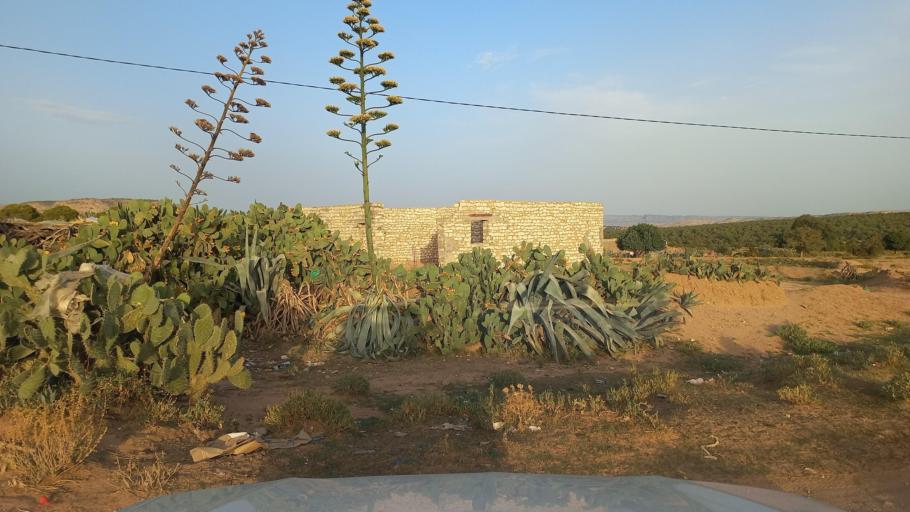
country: TN
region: Al Qasrayn
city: Sbiba
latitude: 35.4131
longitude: 8.9114
